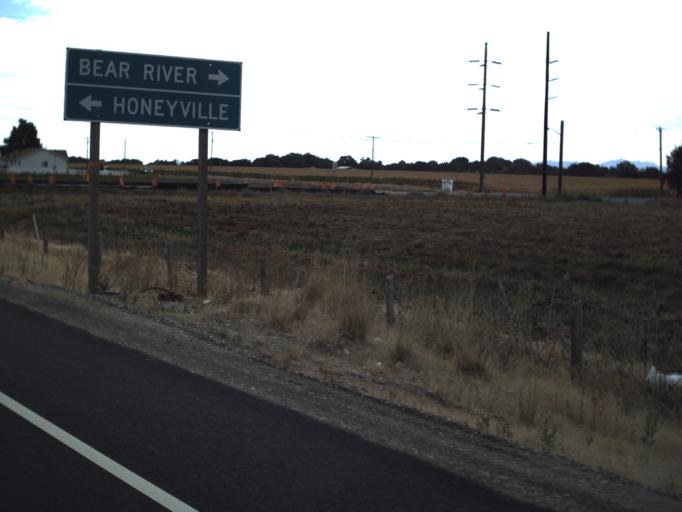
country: US
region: Utah
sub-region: Box Elder County
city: Honeyville
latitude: 41.6344
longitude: -112.1018
